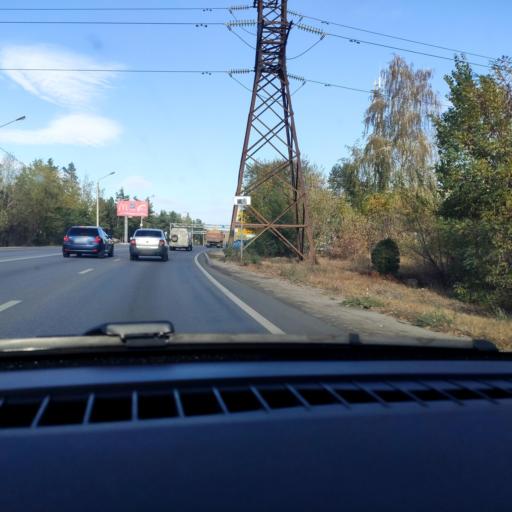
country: RU
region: Voronezj
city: Pridonskoy
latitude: 51.6794
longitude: 39.1152
